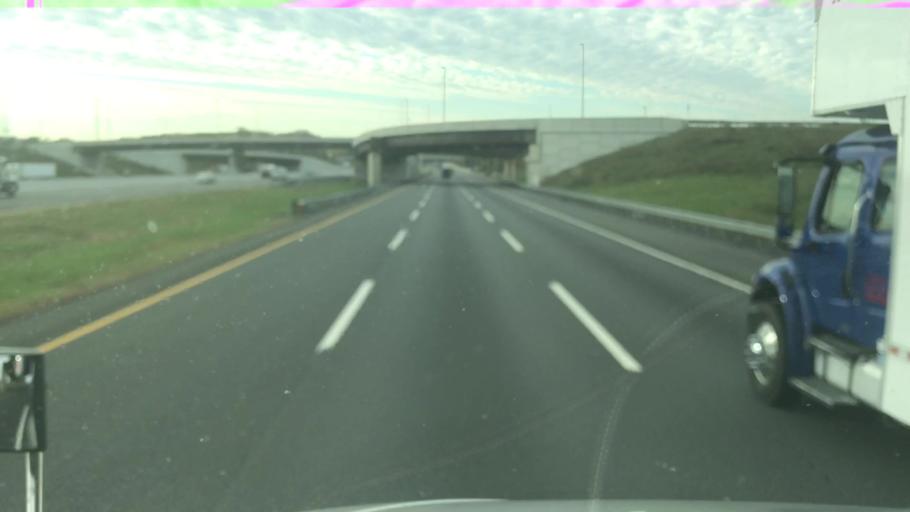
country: US
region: New Jersey
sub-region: Mercer County
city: Hightstown
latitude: 40.2655
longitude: -74.5113
